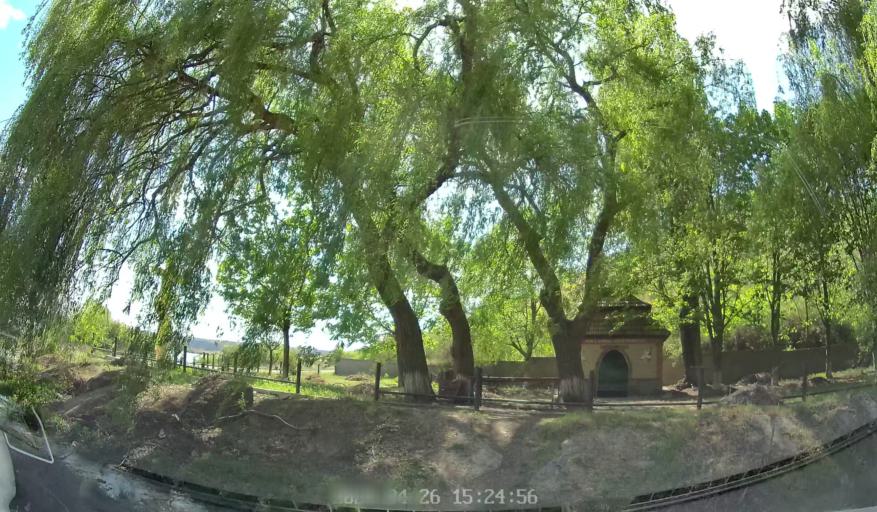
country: MD
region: Telenesti
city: Cocieri
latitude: 47.3651
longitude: 29.0902
